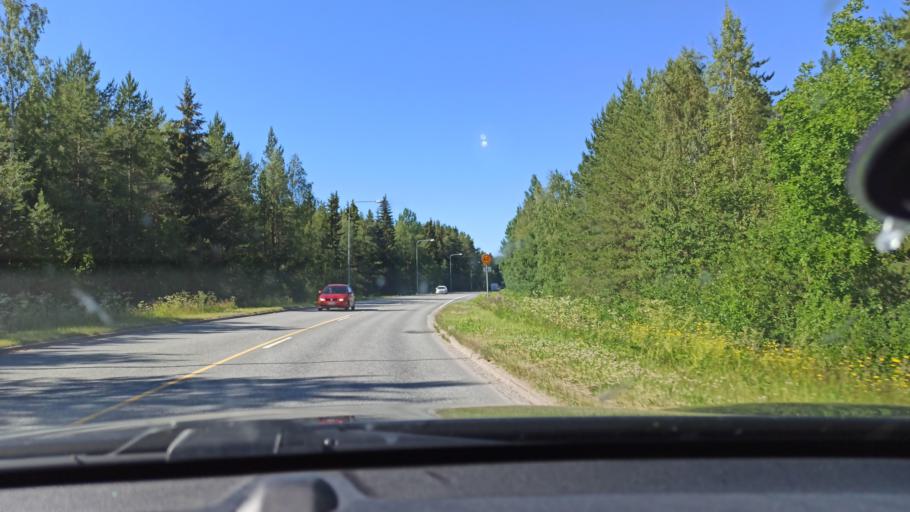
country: FI
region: Ostrobothnia
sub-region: Jakobstadsregionen
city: Jakobstad
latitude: 63.6547
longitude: 22.7141
